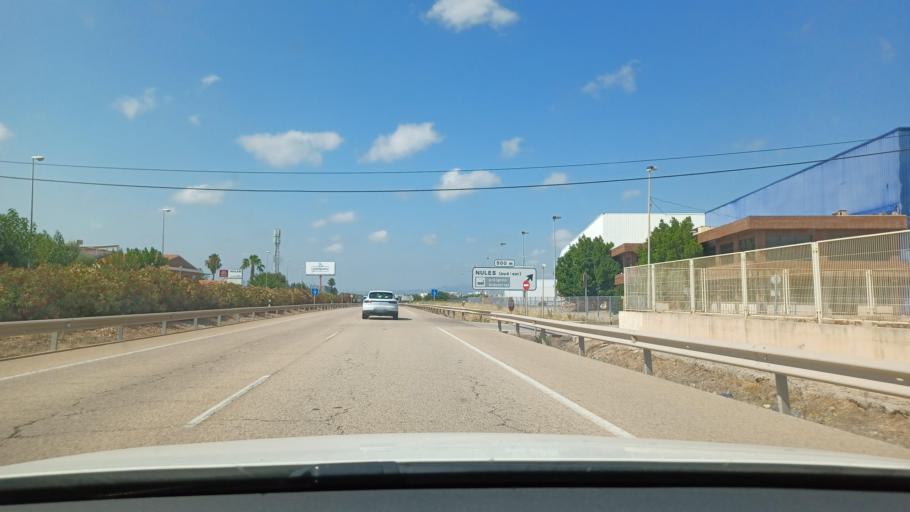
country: ES
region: Valencia
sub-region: Provincia de Castello
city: Moncofar
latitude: 39.8279
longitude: -0.1650
